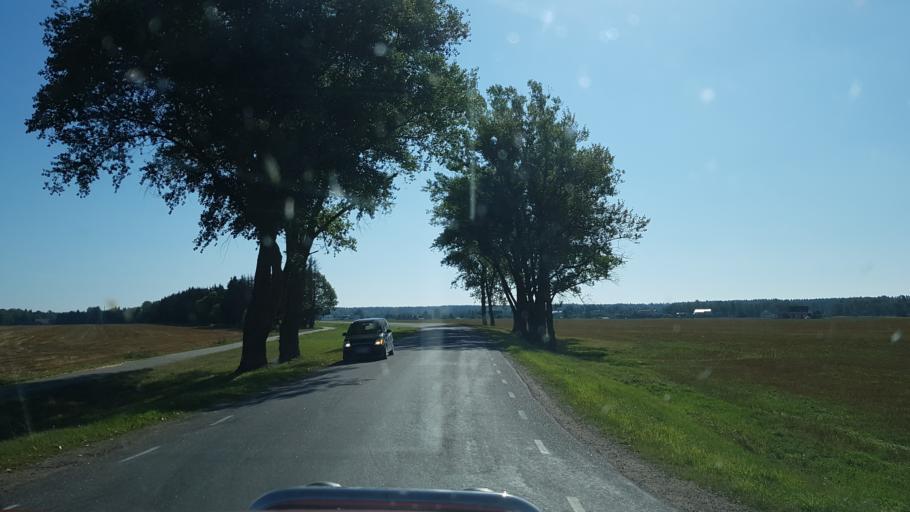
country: EE
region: Tartu
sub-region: Tartu linn
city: Tartu
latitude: 58.3587
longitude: 26.8575
